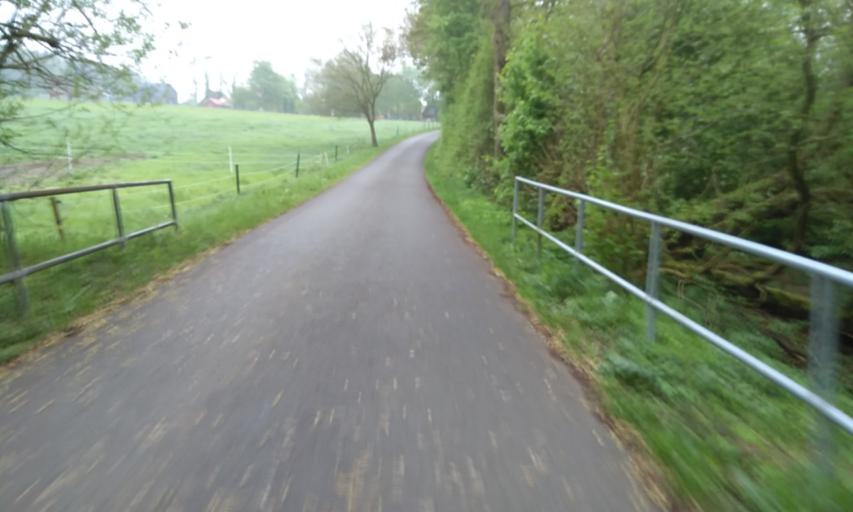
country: DE
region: Lower Saxony
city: Bliedersdorf
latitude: 53.4558
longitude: 9.5568
